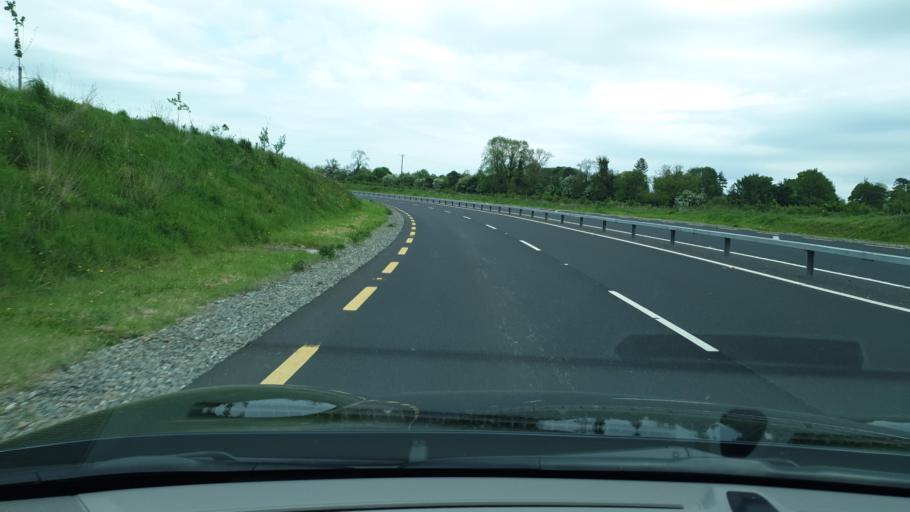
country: IE
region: Leinster
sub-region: Kildare
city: Sallins
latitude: 53.2383
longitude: -6.6774
